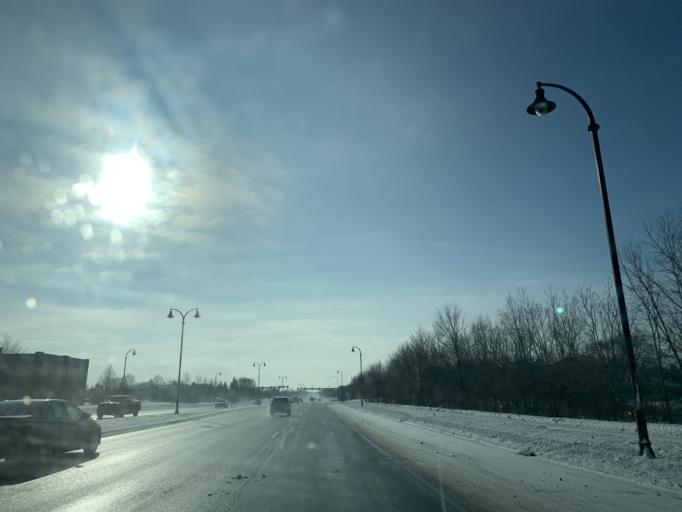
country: US
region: Minnesota
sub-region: Dakota County
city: Apple Valley
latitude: 44.7233
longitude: -93.2178
